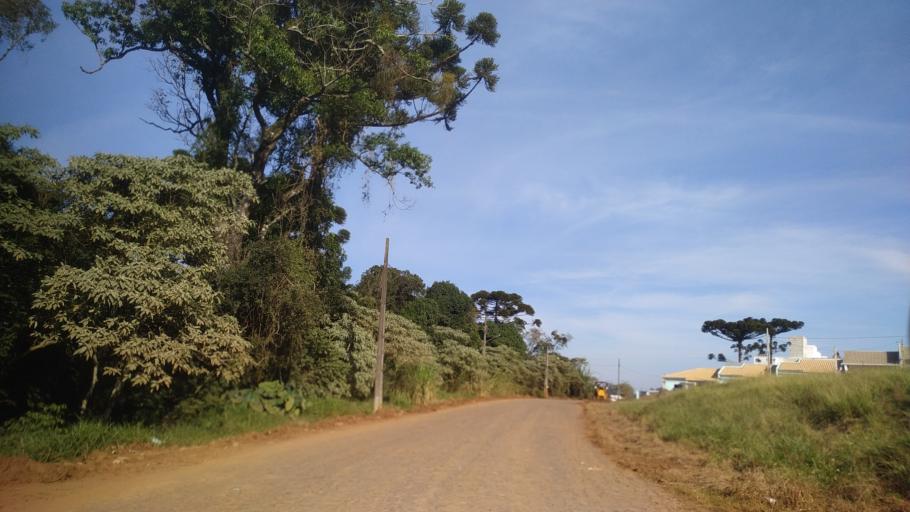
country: BR
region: Santa Catarina
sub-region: Chapeco
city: Chapeco
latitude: -27.1252
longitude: -52.6268
